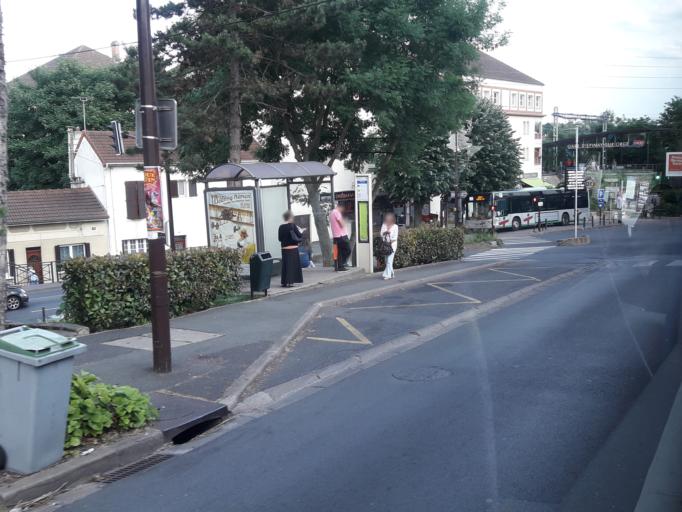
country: FR
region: Ile-de-France
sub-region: Departement de l'Essonne
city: Villemoisson-sur-Orge
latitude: 48.6704
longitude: 2.3323
